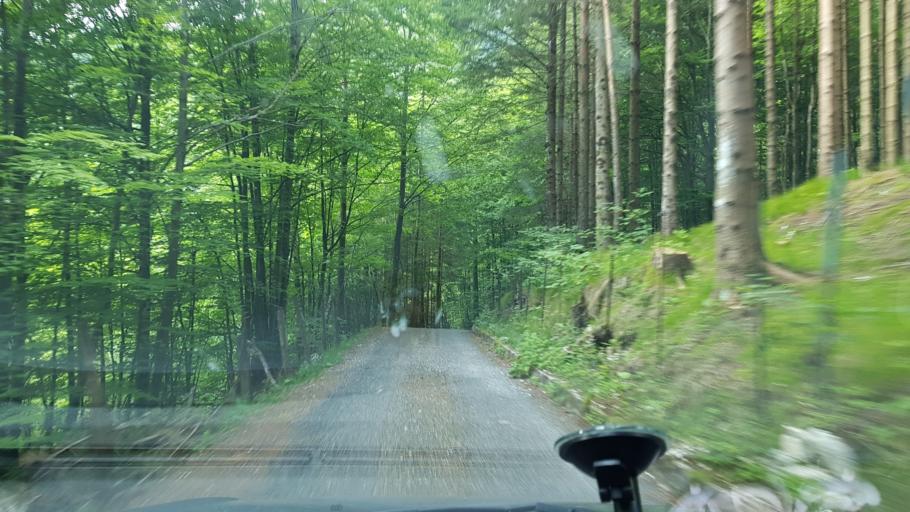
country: IT
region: Friuli Venezia Giulia
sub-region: Provincia di Udine
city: Prato
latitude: 46.3379
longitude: 13.4107
